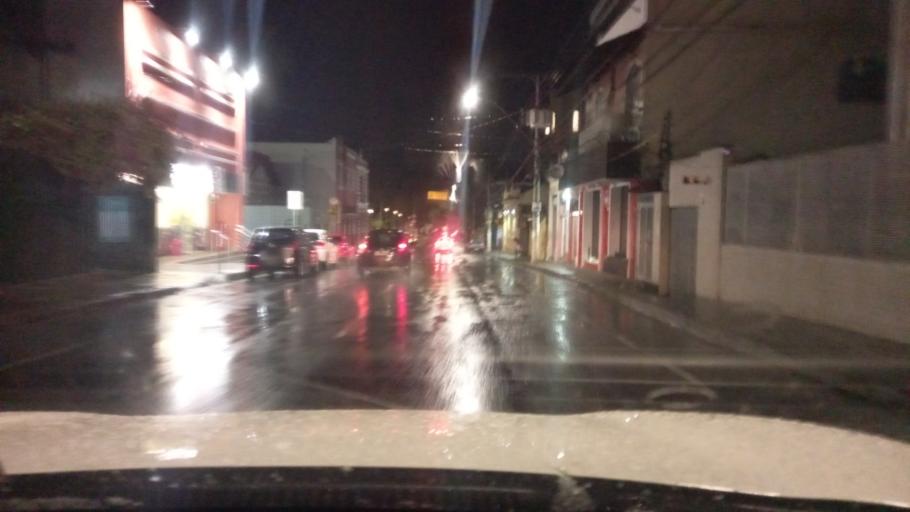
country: BR
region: Minas Gerais
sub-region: Belo Horizonte
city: Belo Horizonte
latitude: -19.9161
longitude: -43.9192
